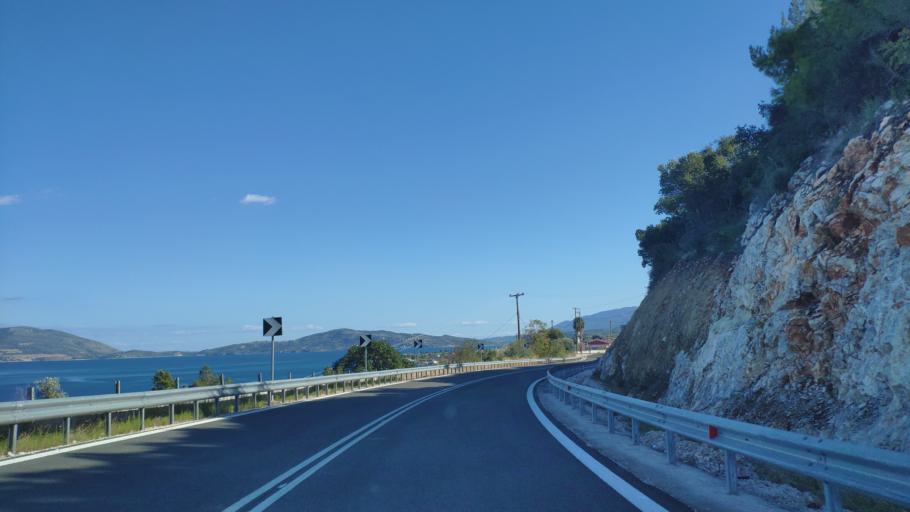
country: GR
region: Peloponnese
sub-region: Nomos Argolidos
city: Didyma
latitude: 37.5529
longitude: 23.2749
